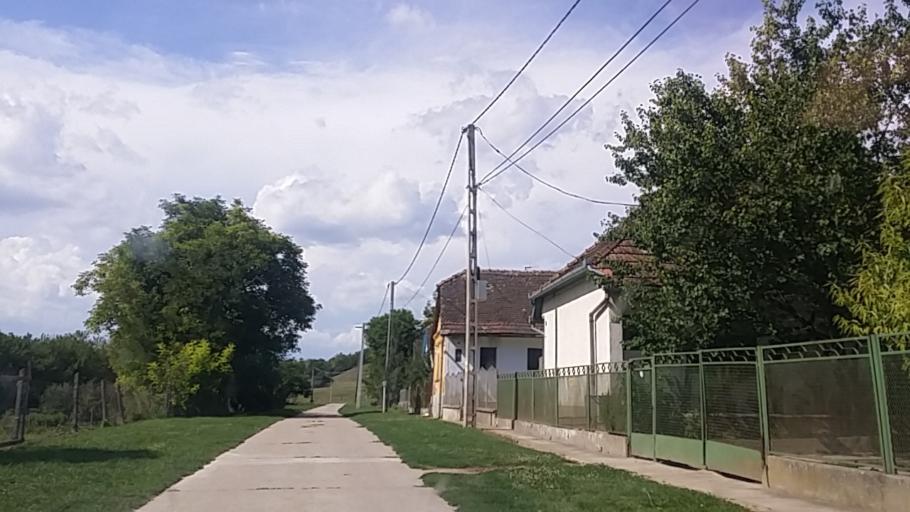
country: HU
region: Tolna
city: Gyonk
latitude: 46.5434
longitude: 18.4692
